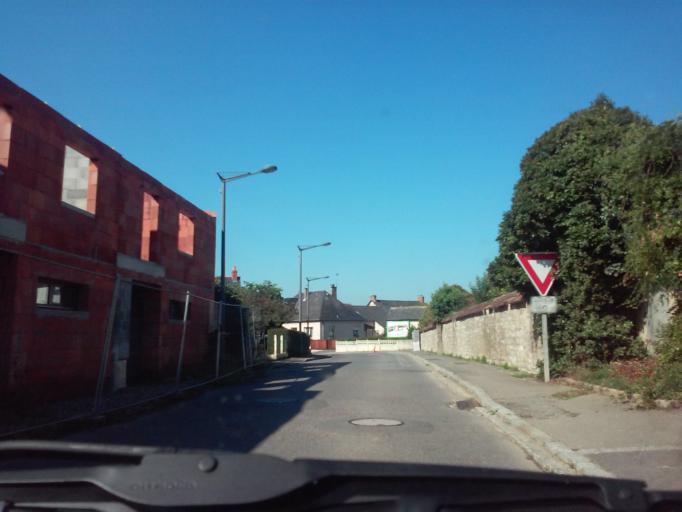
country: FR
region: Brittany
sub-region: Departement d'Ille-et-Vilaine
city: Chevaigne
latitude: 48.2096
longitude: -1.6287
